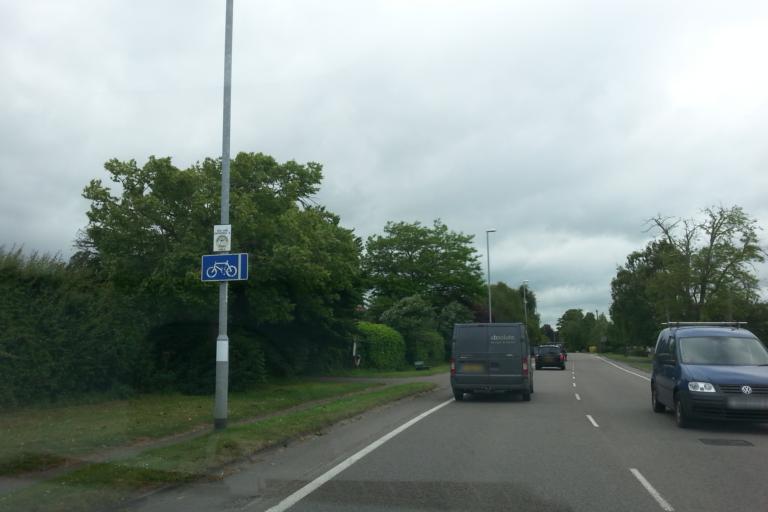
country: GB
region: England
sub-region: Cambridgeshire
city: Cambridge
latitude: 52.1554
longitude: 0.1298
